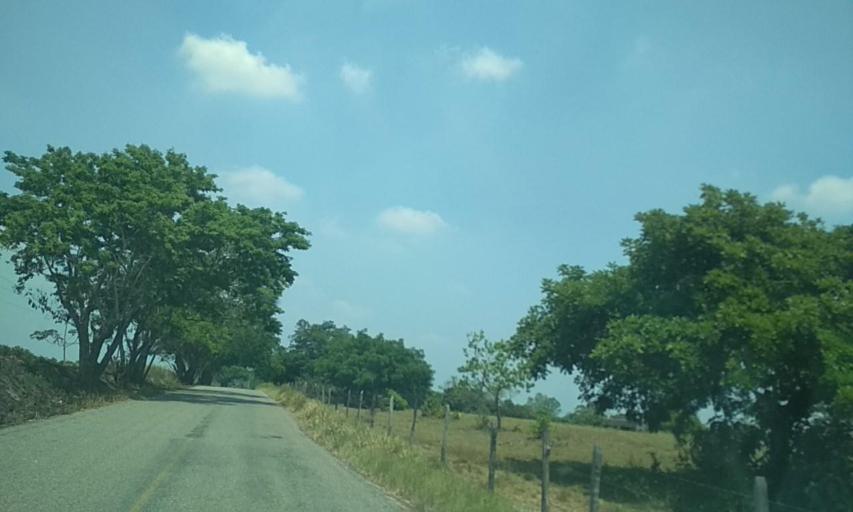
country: MX
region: Tabasco
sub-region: Cardenas
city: Poblado C-33 20 de Noviembre
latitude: 17.8519
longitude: -93.5804
